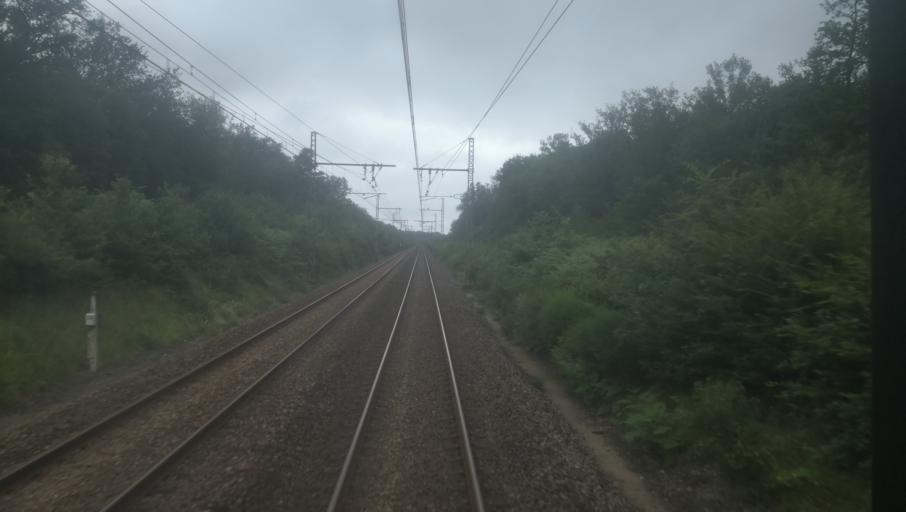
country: FR
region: Centre
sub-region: Departement de l'Indre
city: Luant
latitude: 46.7434
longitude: 1.5935
